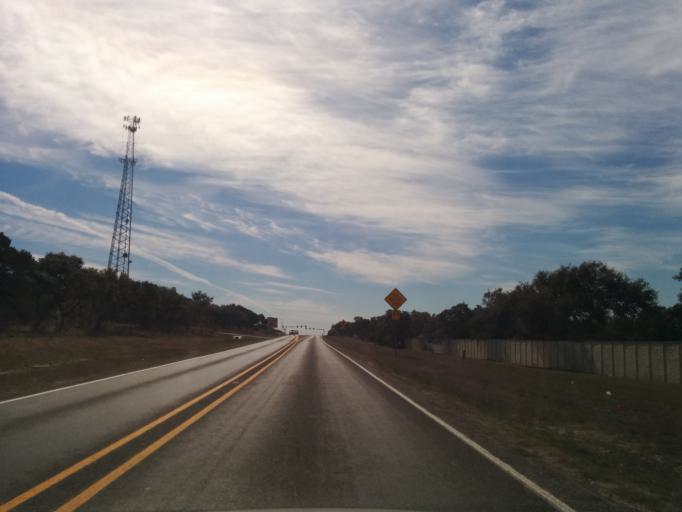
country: US
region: Texas
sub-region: Bexar County
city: Fair Oaks Ranch
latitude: 29.7344
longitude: -98.6235
